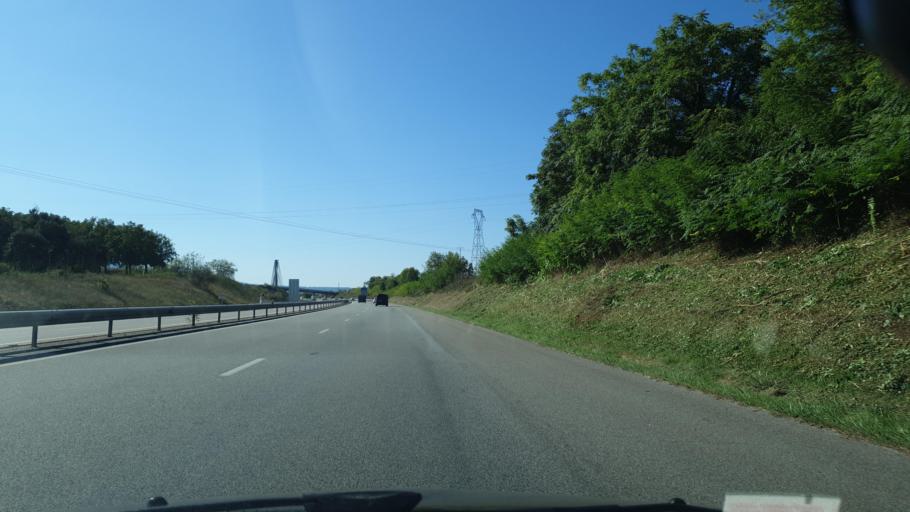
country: FR
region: Rhone-Alpes
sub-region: Departement de l'Isere
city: Saint-Lattier
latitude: 45.0915
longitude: 5.2199
